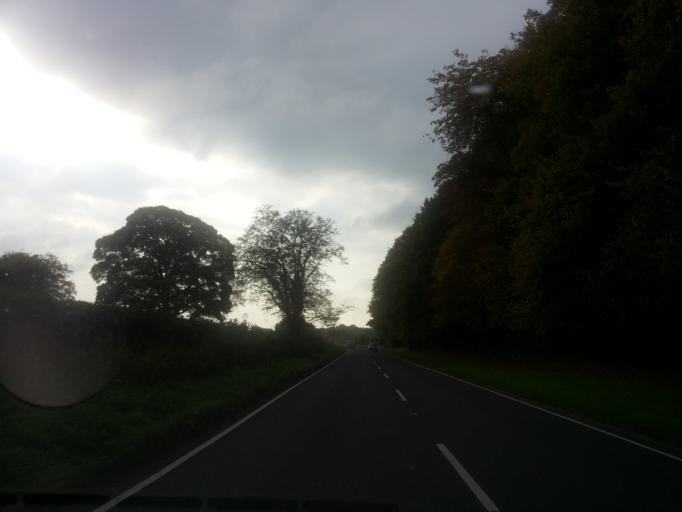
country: GB
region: England
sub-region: Buckinghamshire
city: Great Missenden
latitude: 51.7305
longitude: -0.7270
